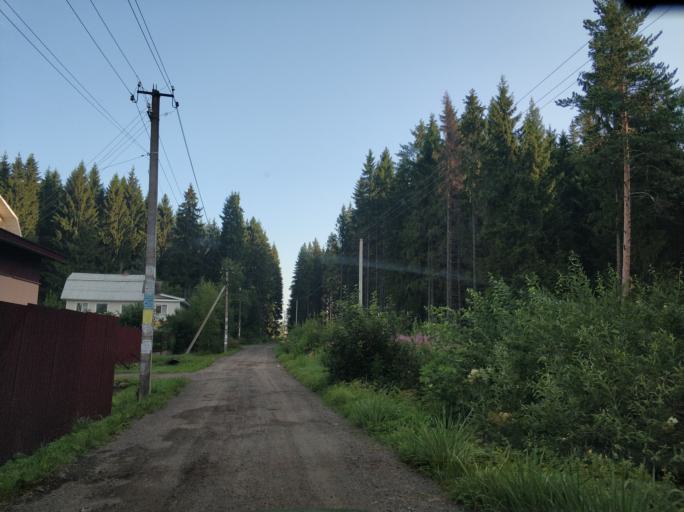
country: RU
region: Leningrad
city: Shcheglovo
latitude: 60.0554
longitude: 30.7495
